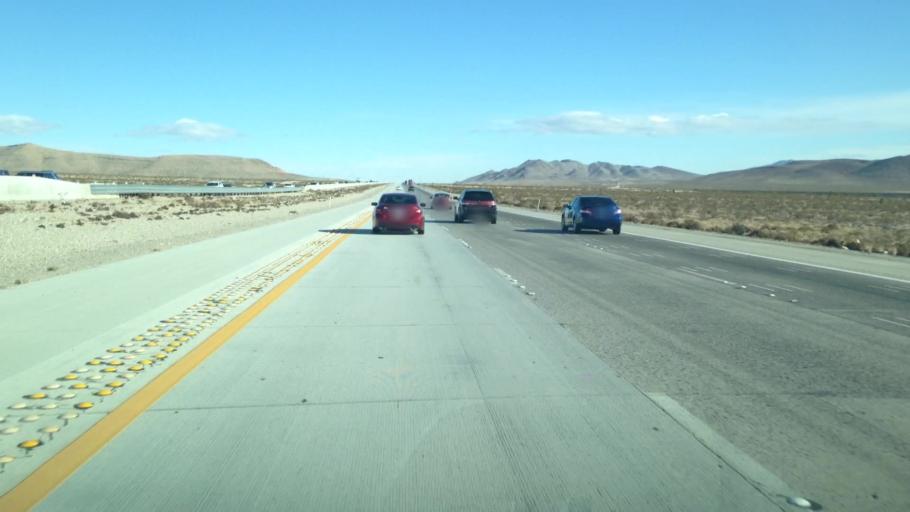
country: US
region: Nevada
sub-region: Clark County
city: Enterprise
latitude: 35.8445
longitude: -115.2732
